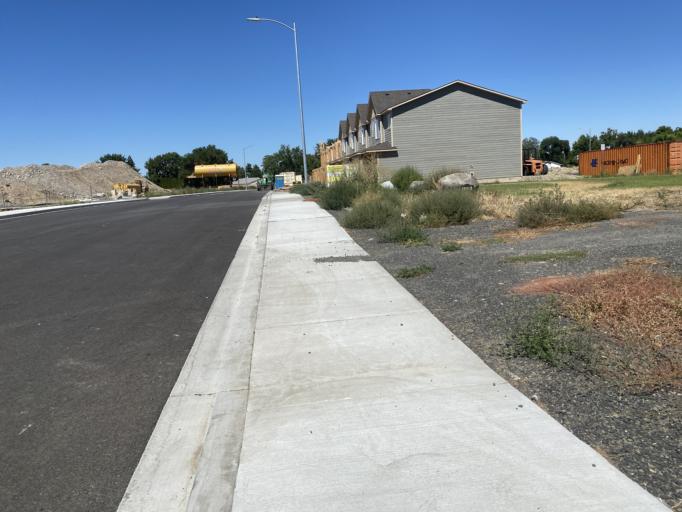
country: US
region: Washington
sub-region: Benton County
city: Kennewick
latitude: 46.2032
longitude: -119.1745
